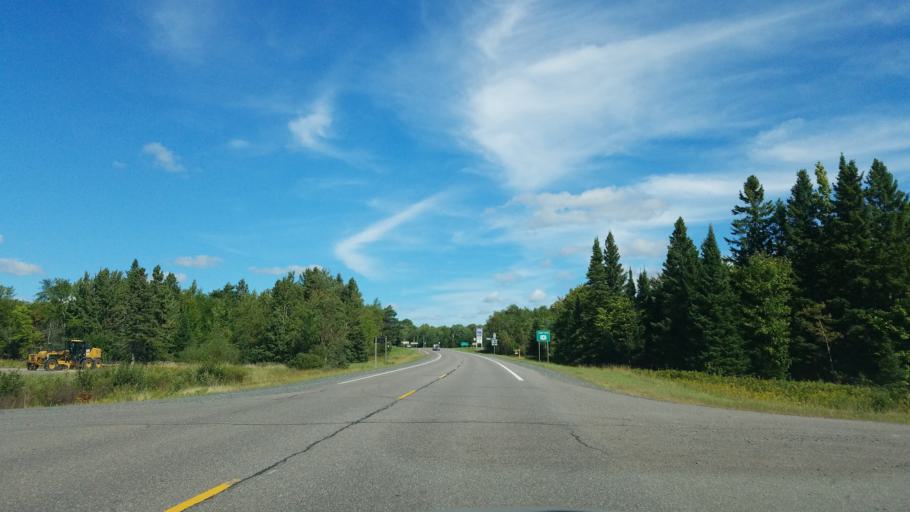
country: US
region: Michigan
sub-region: Baraga County
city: L'Anse
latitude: 46.5457
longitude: -88.5432
